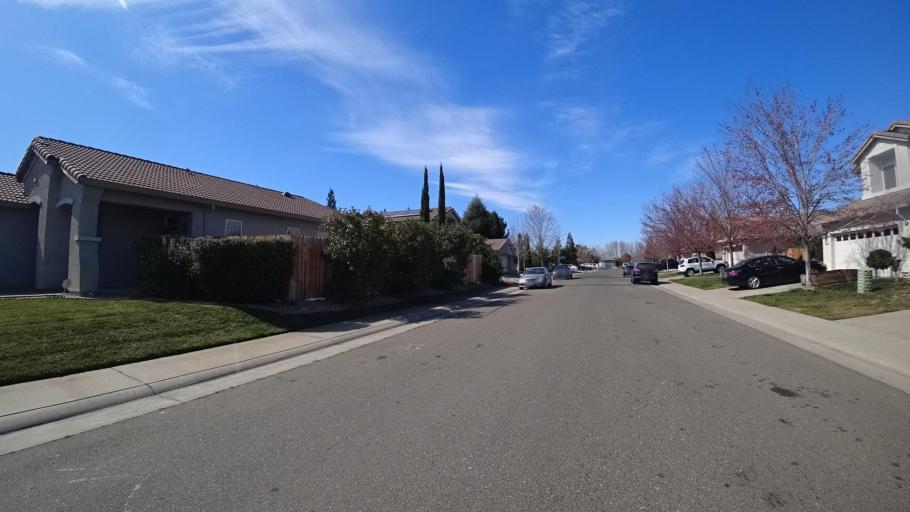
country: US
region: California
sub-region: Sacramento County
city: Rancho Cordova
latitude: 38.5731
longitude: -121.2765
